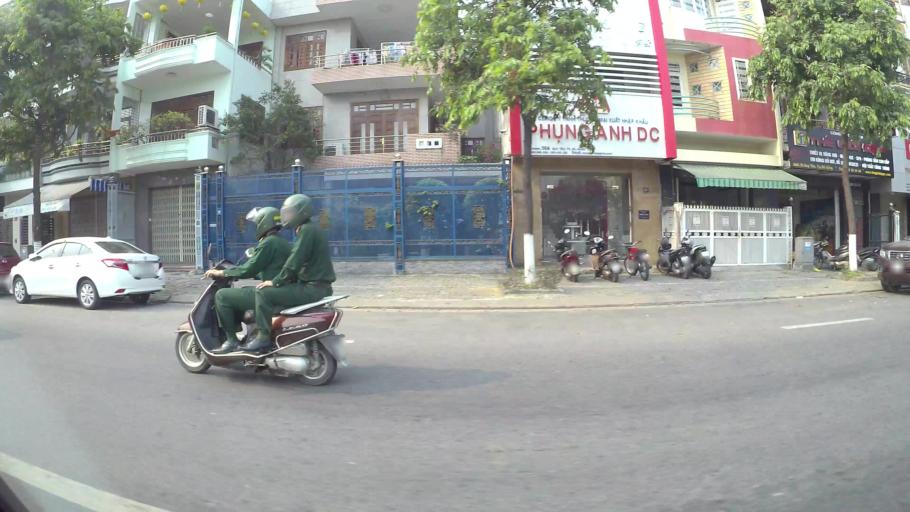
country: VN
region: Da Nang
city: Son Tra
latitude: 16.0490
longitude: 108.2175
